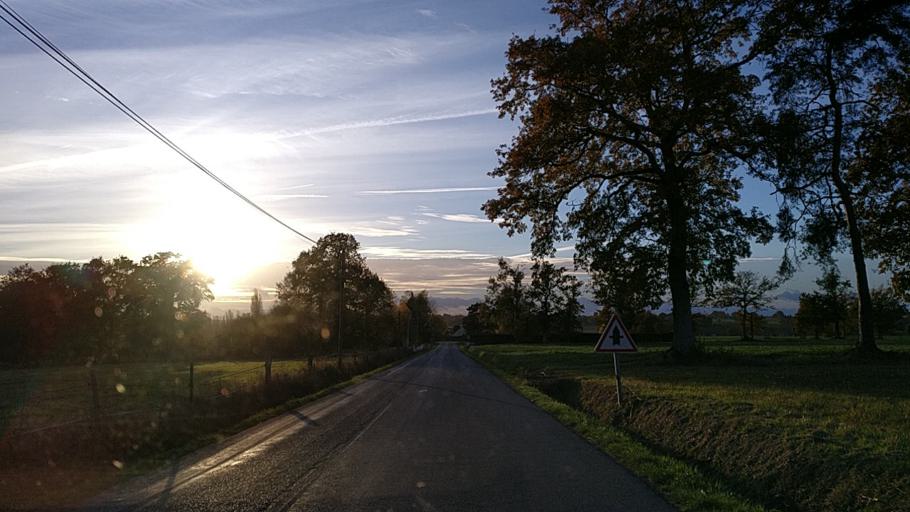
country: FR
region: Brittany
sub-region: Departement d'Ille-et-Vilaine
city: Saint-Sulpice-la-Foret
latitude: 48.2164
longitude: -1.5934
